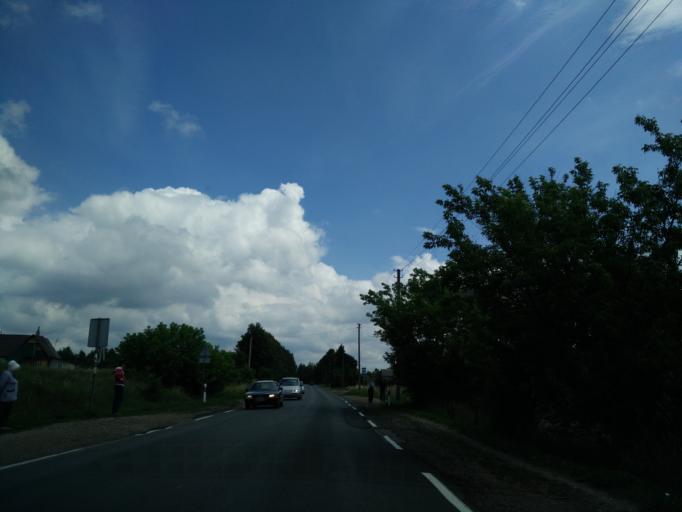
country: LT
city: Skaidiskes
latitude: 54.6925
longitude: 25.4590
